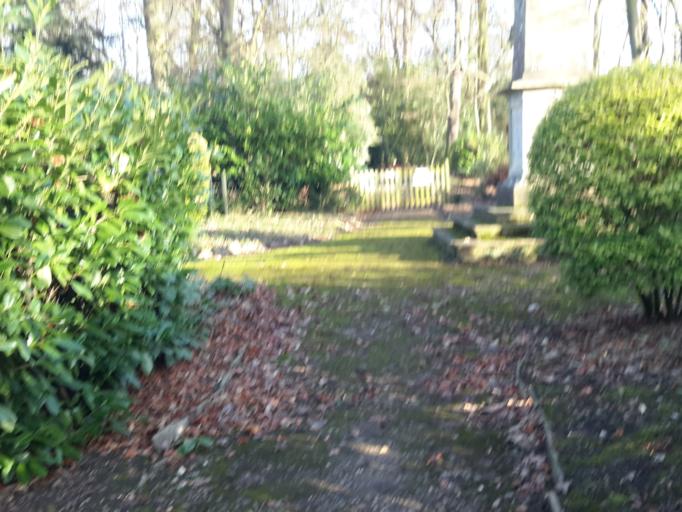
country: GB
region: England
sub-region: Worcestershire
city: Evesham
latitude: 52.1078
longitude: -1.9523
